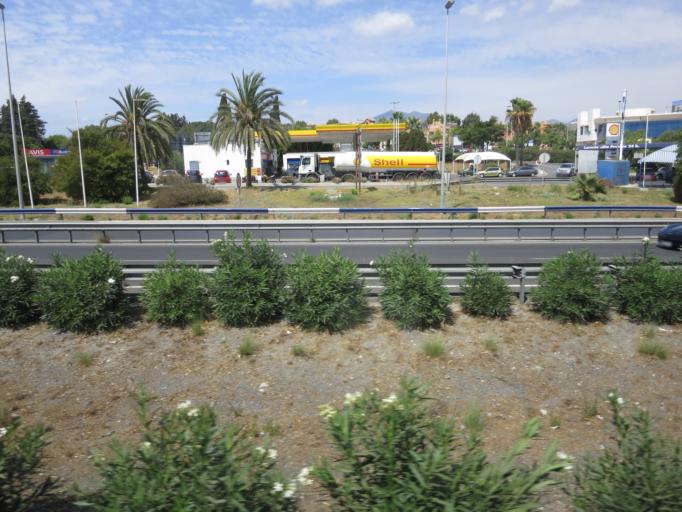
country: ES
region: Andalusia
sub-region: Provincia de Malaga
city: Marbella
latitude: 36.4942
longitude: -4.9509
